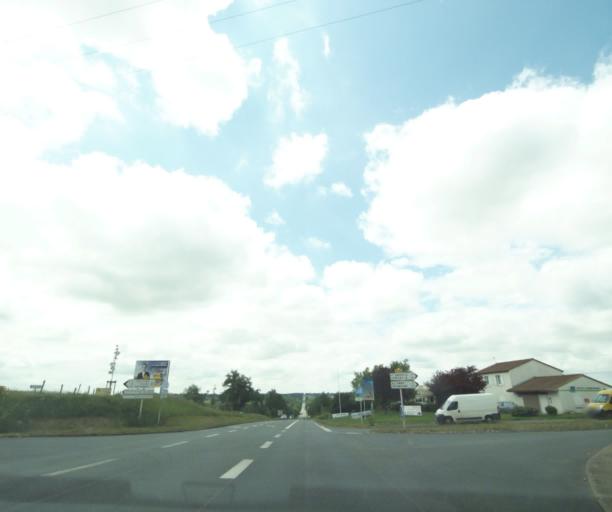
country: FR
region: Poitou-Charentes
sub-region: Departement des Deux-Sevres
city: Saint-Pardoux
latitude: 46.5696
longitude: -0.2982
